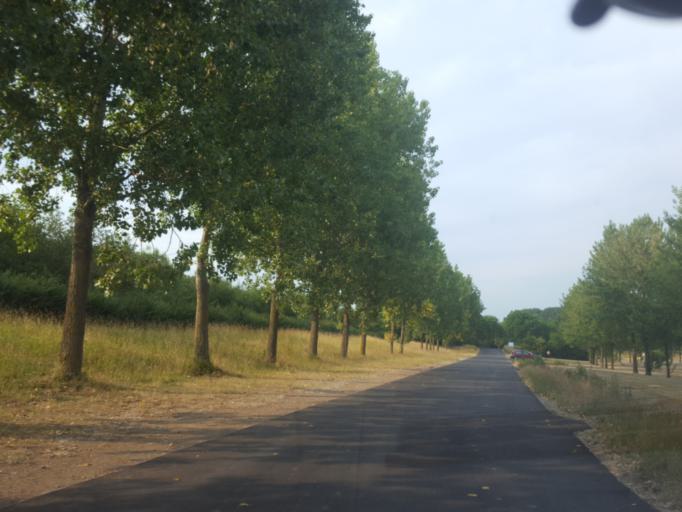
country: NL
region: Limburg
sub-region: Gemeente Maasgouw
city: Maasbracht
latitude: 51.1544
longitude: 5.8420
